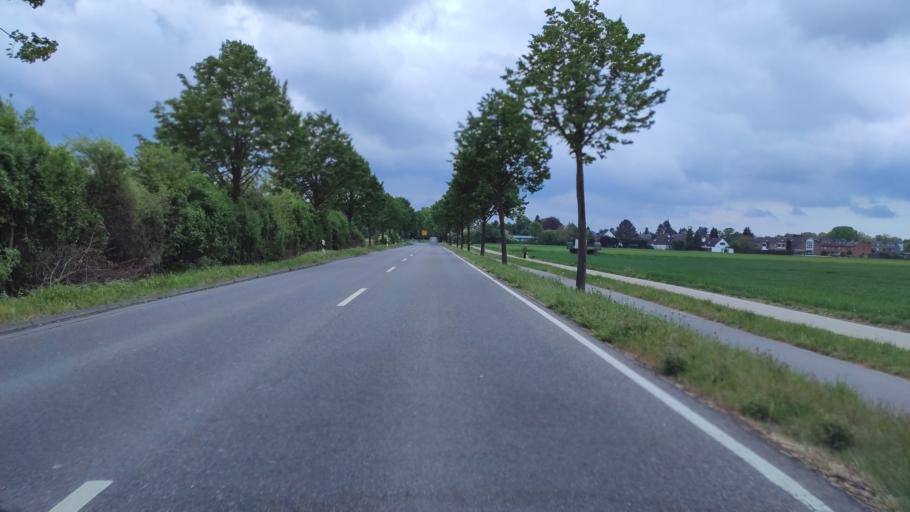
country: DE
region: North Rhine-Westphalia
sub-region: Regierungsbezirk Dusseldorf
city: Kaarst
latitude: 51.2036
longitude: 6.6180
